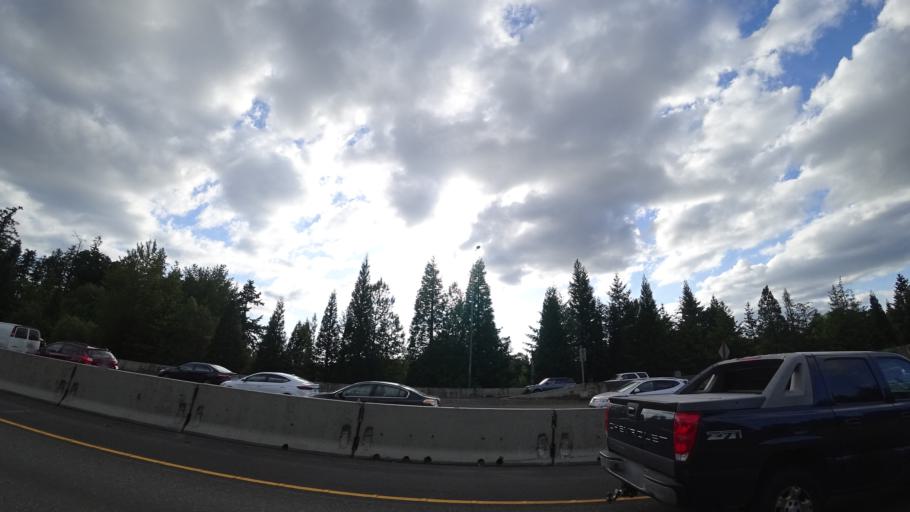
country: US
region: Oregon
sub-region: Washington County
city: Cedar Hills
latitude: 45.4971
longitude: -122.7910
